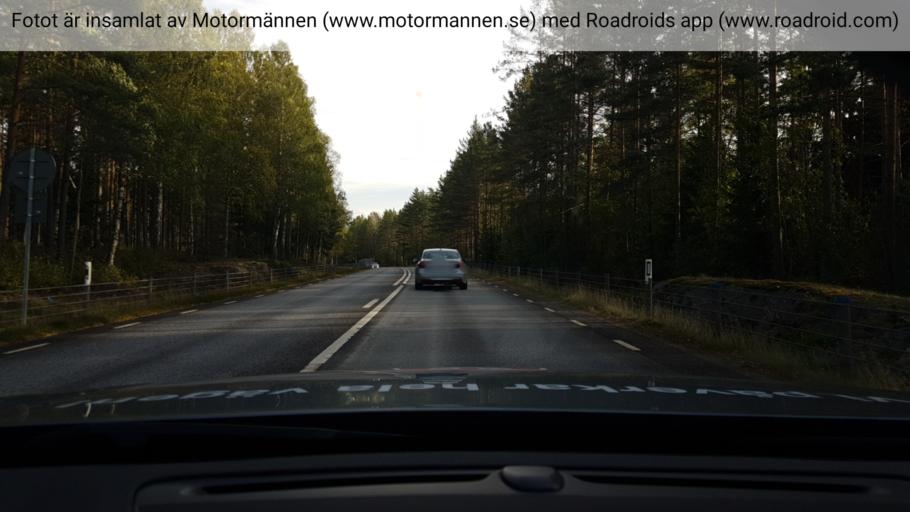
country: SE
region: Vaermland
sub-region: Arjangs Kommun
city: Toecksfors
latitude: 59.4781
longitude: 11.9574
